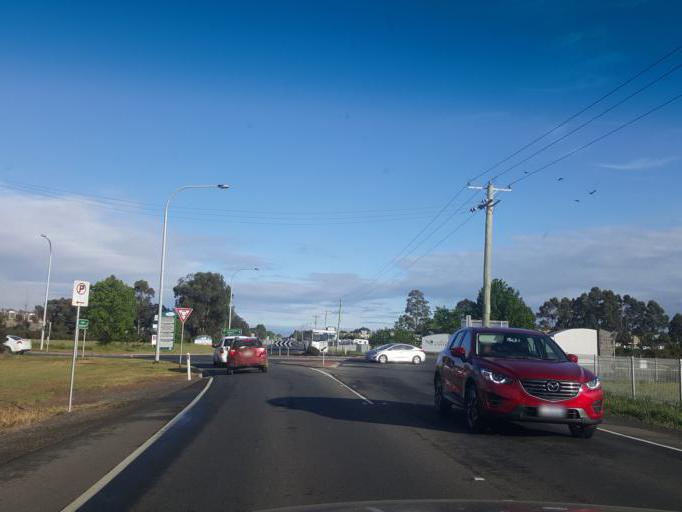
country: AU
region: Tasmania
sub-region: Northern Midlands
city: Perth
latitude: -41.5418
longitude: 147.2017
